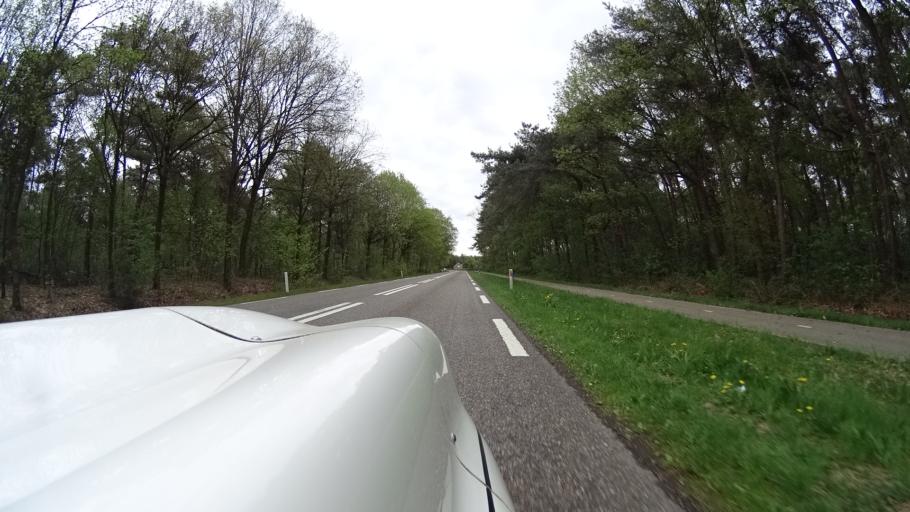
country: NL
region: North Brabant
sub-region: Gemeente Boxmeer
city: Overloon
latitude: 51.5398
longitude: 5.9171
